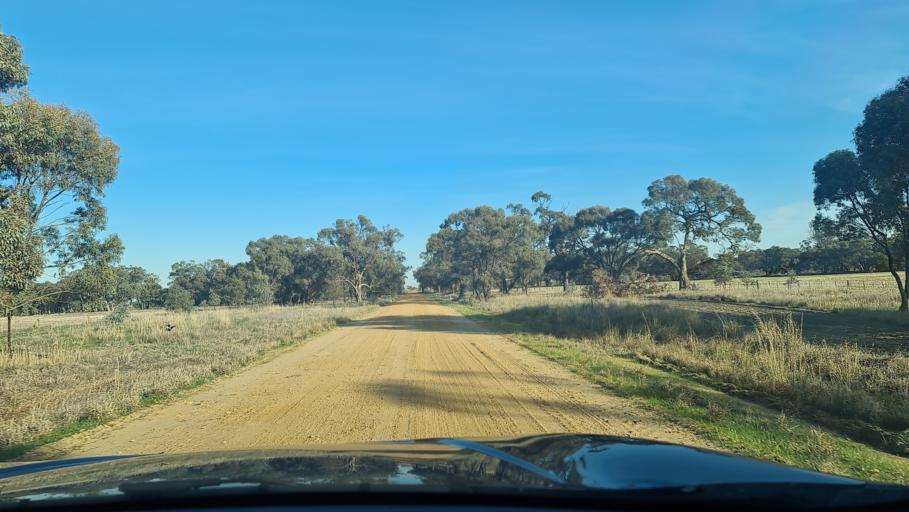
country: AU
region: Victoria
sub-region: Horsham
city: Horsham
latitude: -36.3538
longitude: 142.3997
